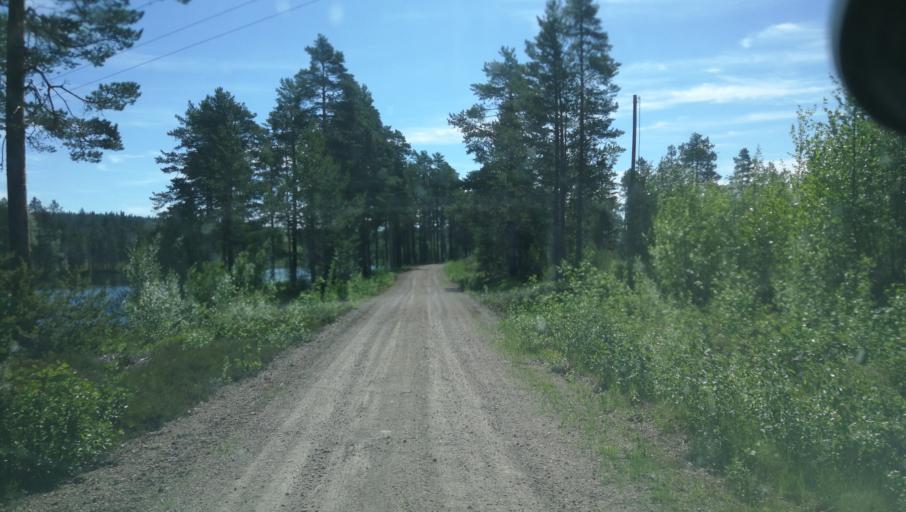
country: SE
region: Dalarna
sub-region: Vansbro Kommun
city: Vansbro
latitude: 60.8255
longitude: 14.1864
